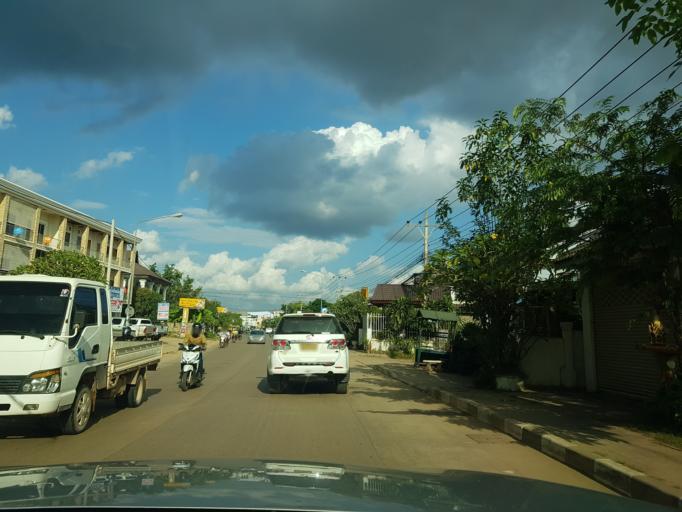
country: TH
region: Nong Khai
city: Si Chiang Mai
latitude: 17.9738
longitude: 102.5546
